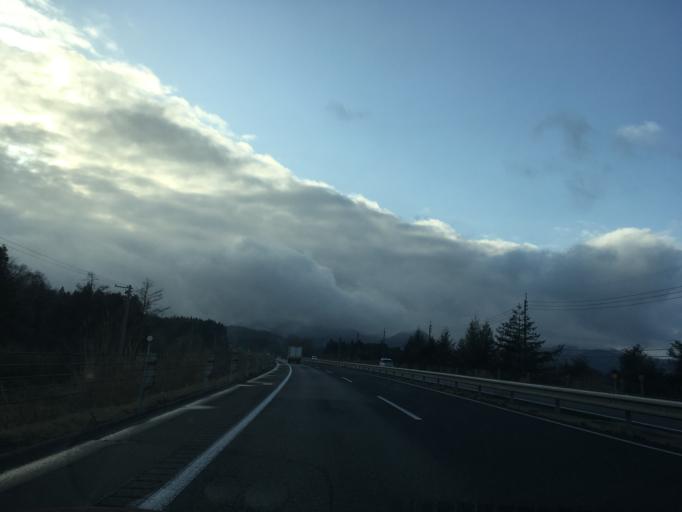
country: JP
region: Miyagi
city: Okawara
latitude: 38.1726
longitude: 140.6331
